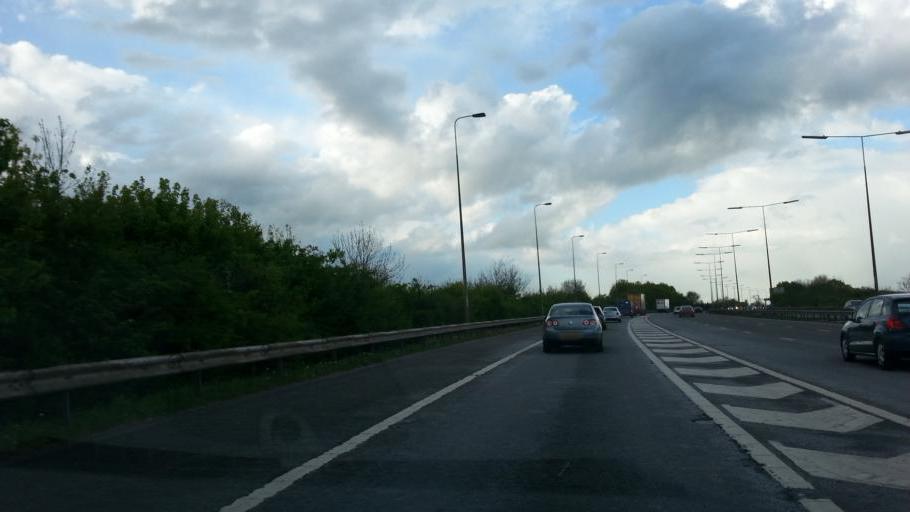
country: GB
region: England
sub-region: Warwickshire
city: Bedworth
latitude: 52.4445
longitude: -1.4257
